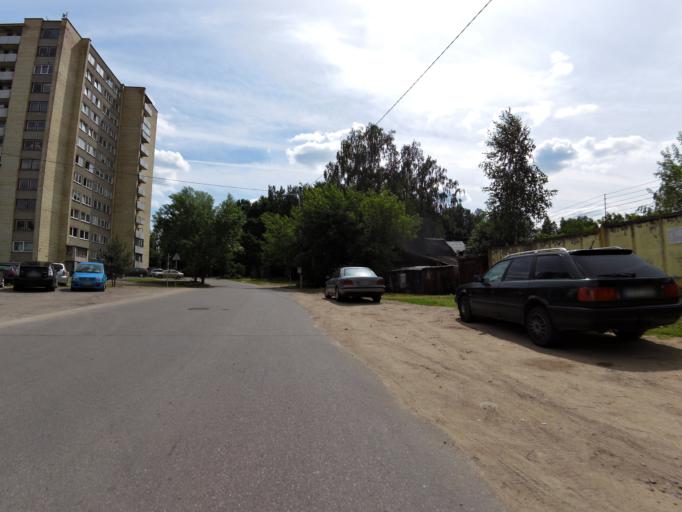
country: LT
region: Vilnius County
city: Rasos
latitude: 54.6760
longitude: 25.3179
